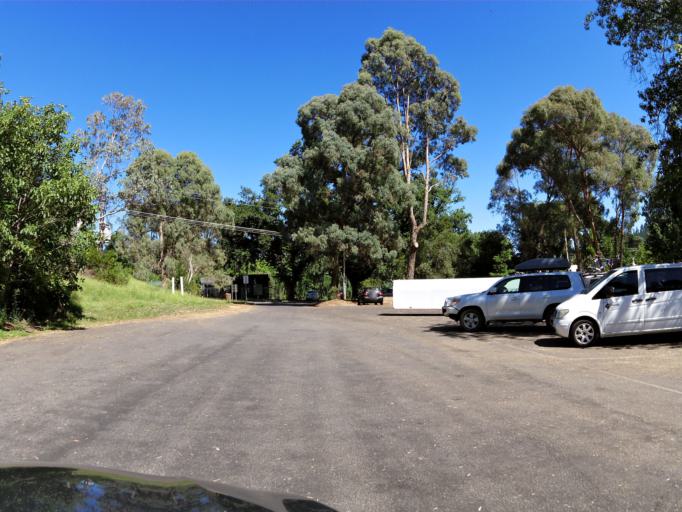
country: AU
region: Victoria
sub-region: Alpine
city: Mount Beauty
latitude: -36.7307
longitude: 146.9617
